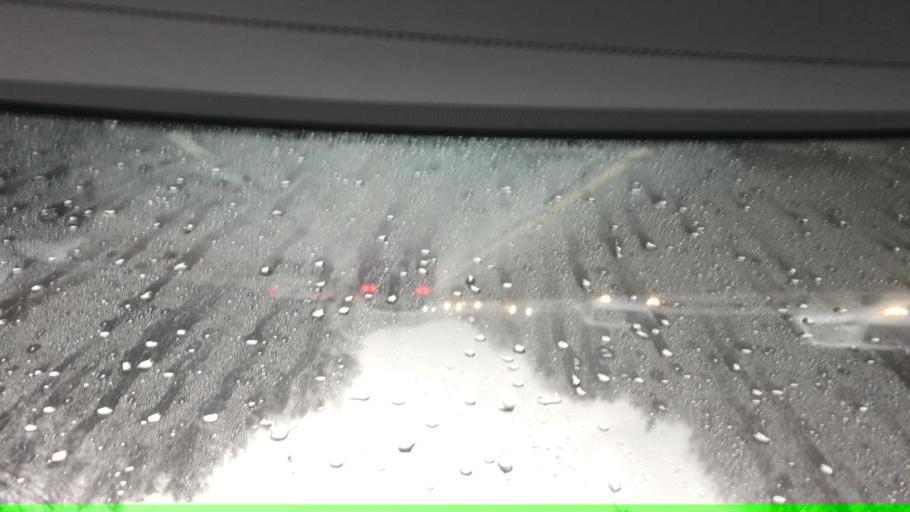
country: US
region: Connecticut
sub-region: New Haven County
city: Hamden
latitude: 41.3678
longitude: -72.9167
